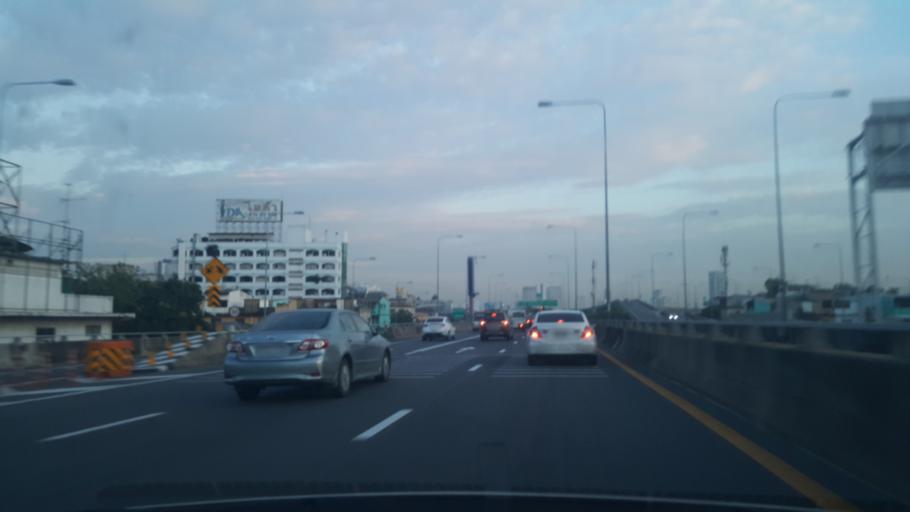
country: TH
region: Bangkok
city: Sathon
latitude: 13.6961
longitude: 100.5241
